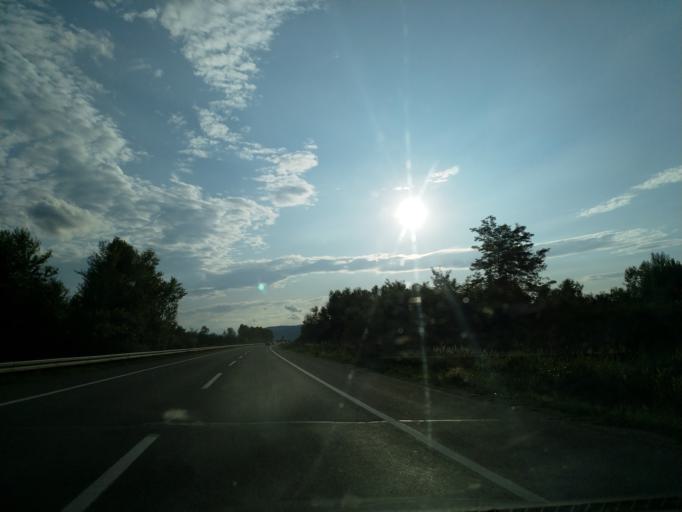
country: RS
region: Central Serbia
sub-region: Rasinski Okrug
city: Krusevac
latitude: 43.6095
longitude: 21.3367
